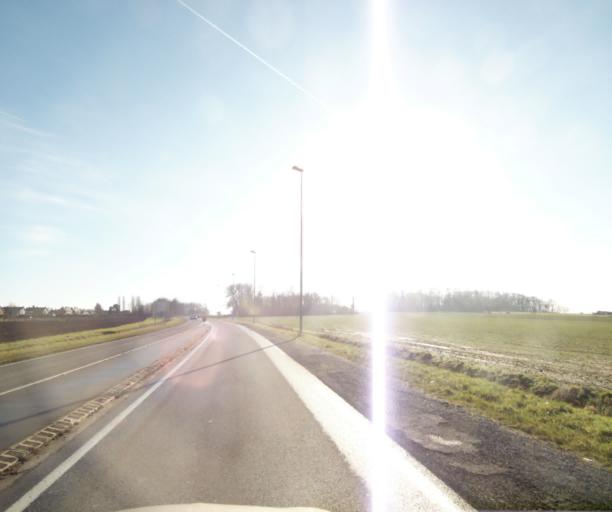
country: FR
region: Nord-Pas-de-Calais
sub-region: Departement du Nord
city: Famars
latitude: 50.3131
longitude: 3.5138
